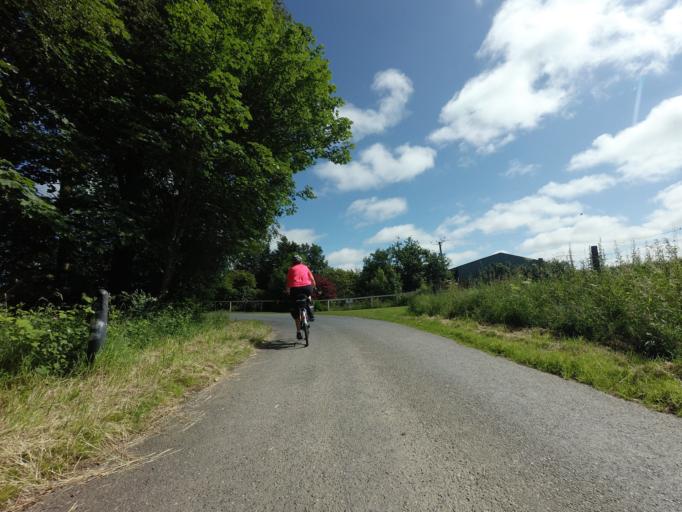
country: GB
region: Scotland
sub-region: Aberdeenshire
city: Turriff
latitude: 57.5884
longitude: -2.5042
